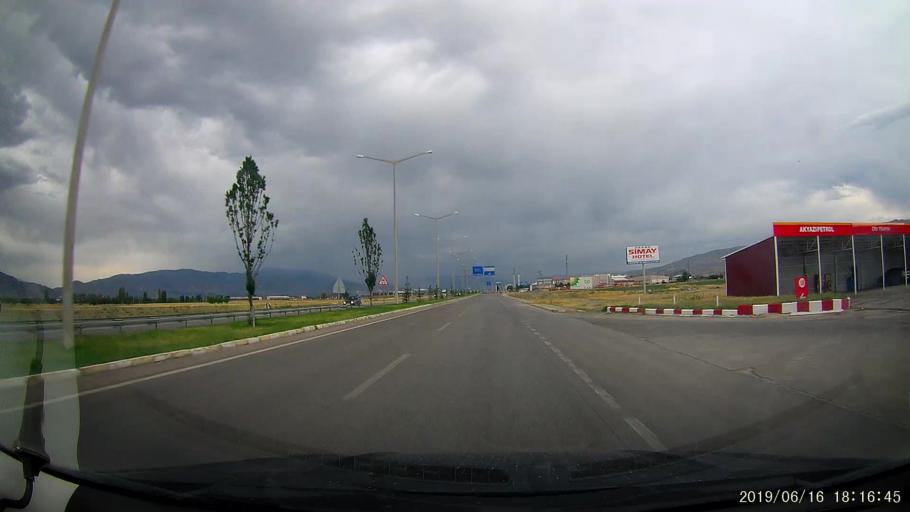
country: TR
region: Erzincan
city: Erzincan
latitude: 39.7302
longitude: 39.5434
